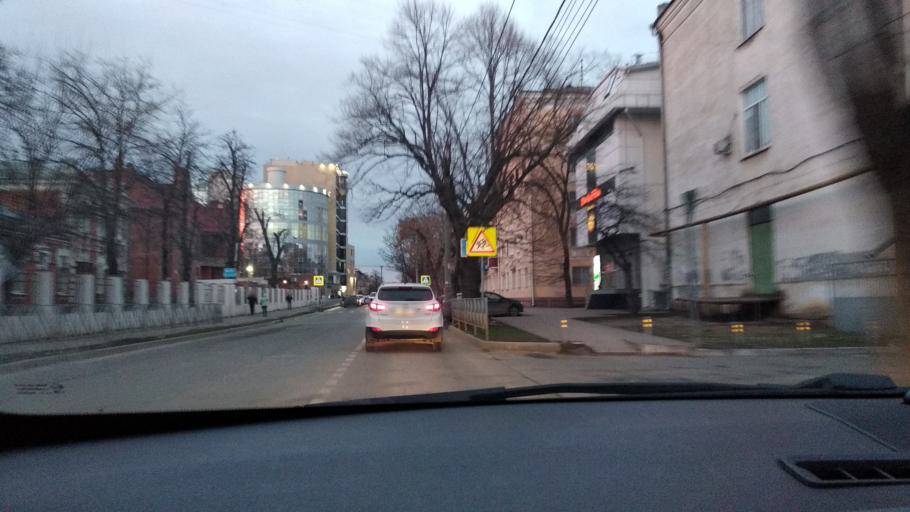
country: RU
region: Krasnodarskiy
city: Krasnodar
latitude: 45.0438
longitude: 38.9747
